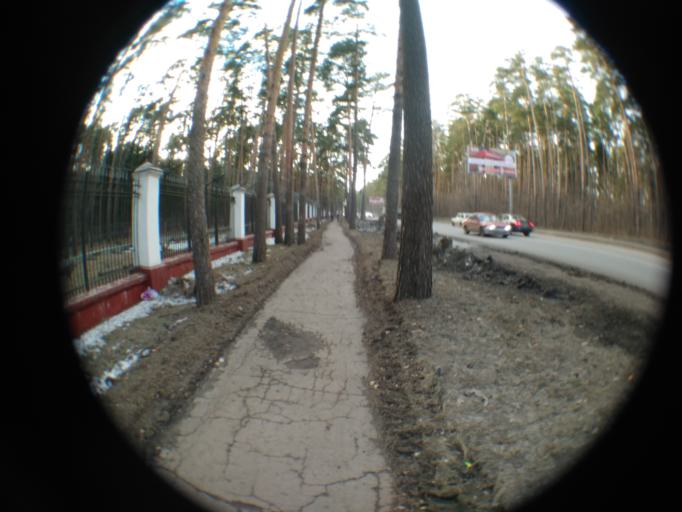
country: RU
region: Moskovskaya
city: Kratovo
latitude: 55.5760
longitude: 38.1635
